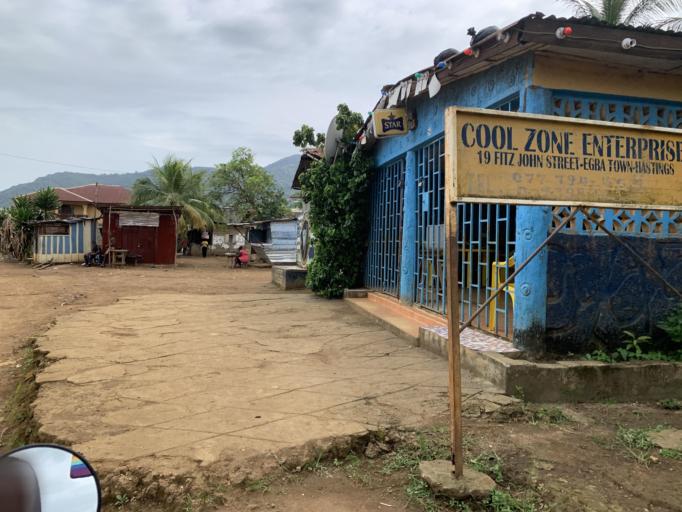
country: SL
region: Western Area
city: Hastings
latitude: 8.3772
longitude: -13.1339
